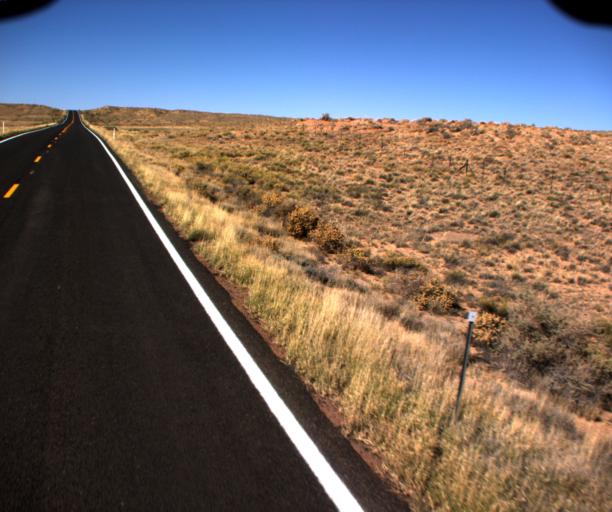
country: US
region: Arizona
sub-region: Coconino County
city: Tuba City
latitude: 35.9550
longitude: -110.9288
